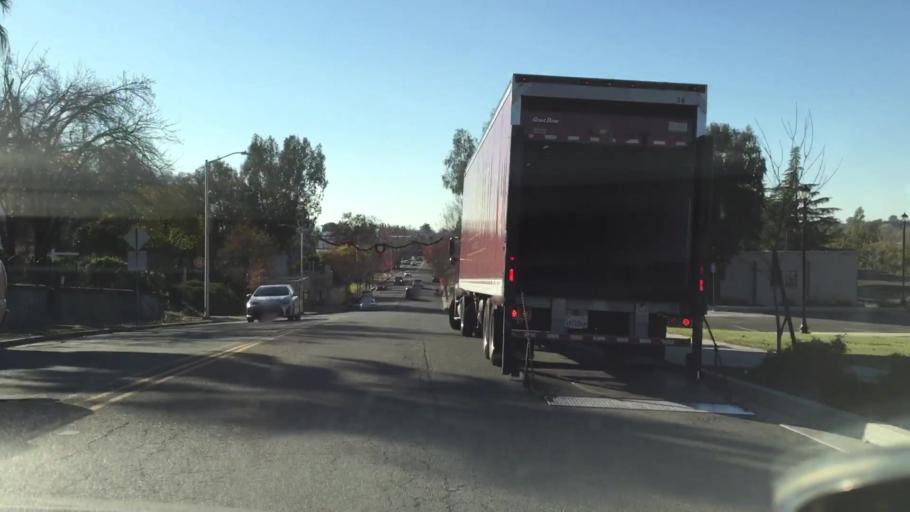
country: US
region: California
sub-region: Butte County
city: Oroville
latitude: 39.5159
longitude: -121.5503
